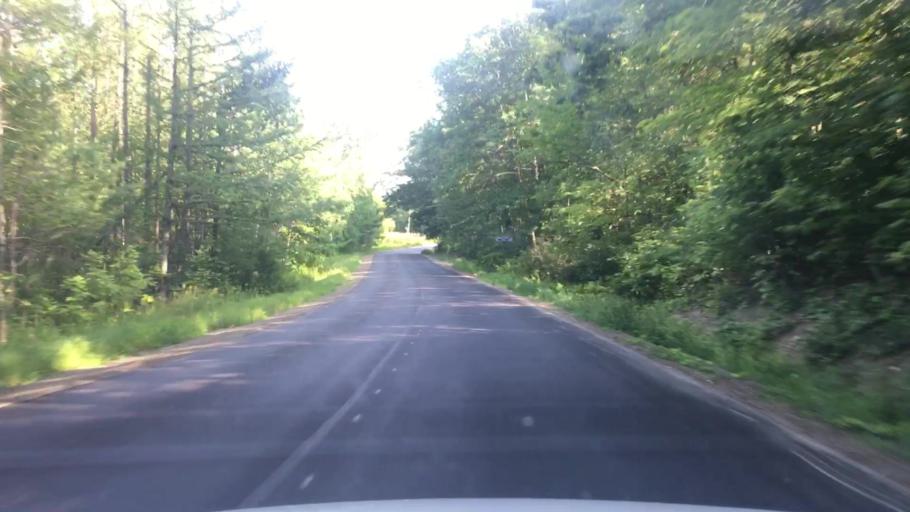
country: US
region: Maine
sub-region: Kennebec County
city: Waterville
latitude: 44.5688
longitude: -69.6540
